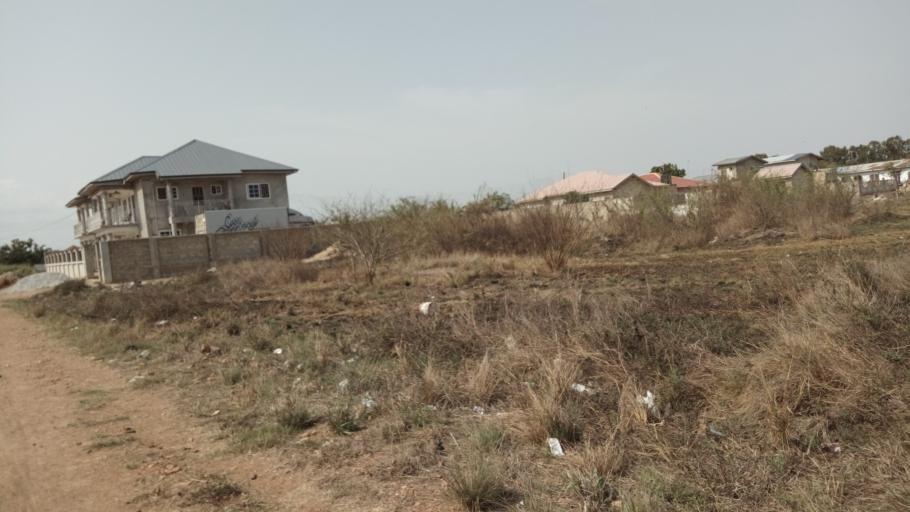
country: GH
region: Central
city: Winneba
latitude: 5.3713
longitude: -0.6487
